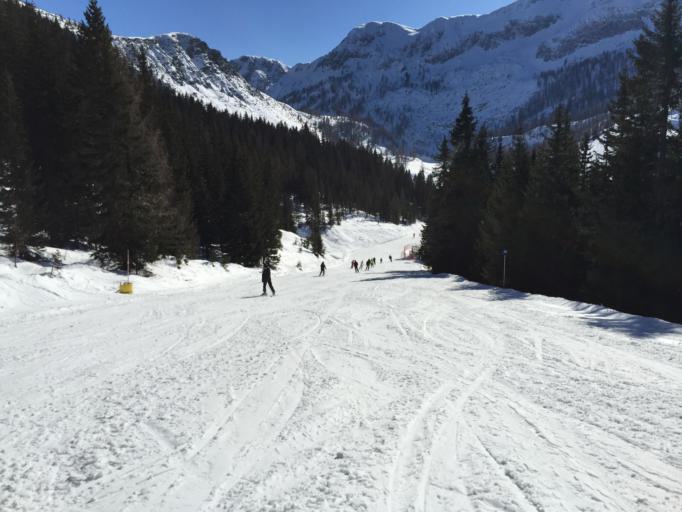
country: AT
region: Salzburg
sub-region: Politischer Bezirk Sankt Johann im Pongau
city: Untertauern
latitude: 47.2870
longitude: 13.4663
